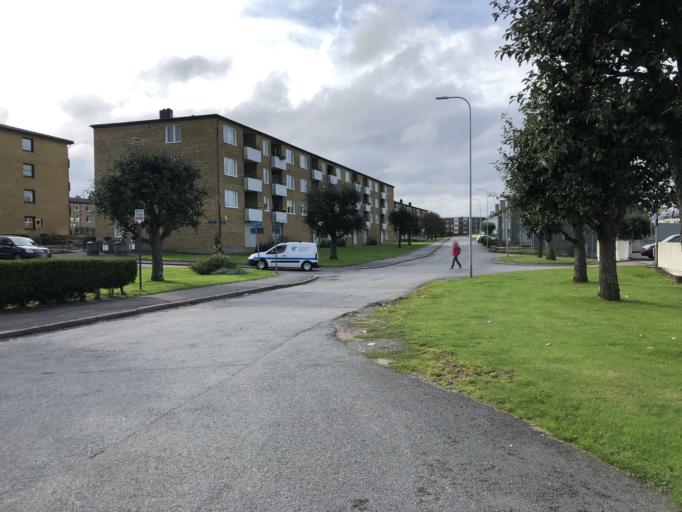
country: SE
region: Vaestra Goetaland
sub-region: Goteborg
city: Majorna
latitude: 57.7356
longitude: 11.8886
